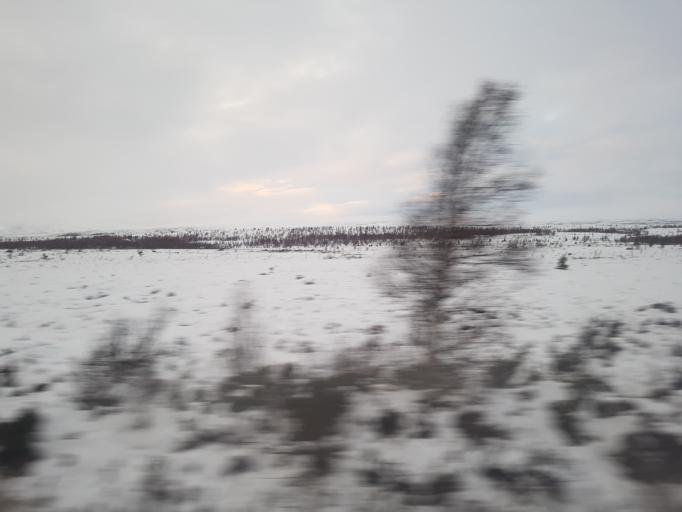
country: NO
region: Oppland
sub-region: Dovre
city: Dovre
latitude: 62.1384
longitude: 9.3223
